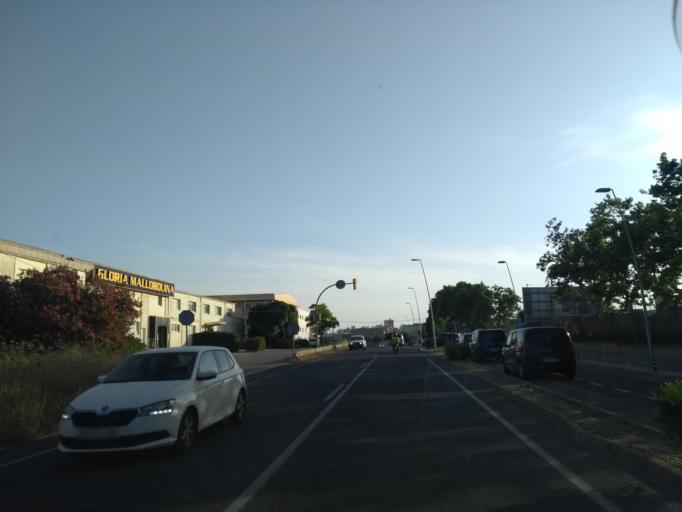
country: ES
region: Balearic Islands
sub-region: Illes Balears
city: Inca
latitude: 39.7276
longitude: 2.9245
